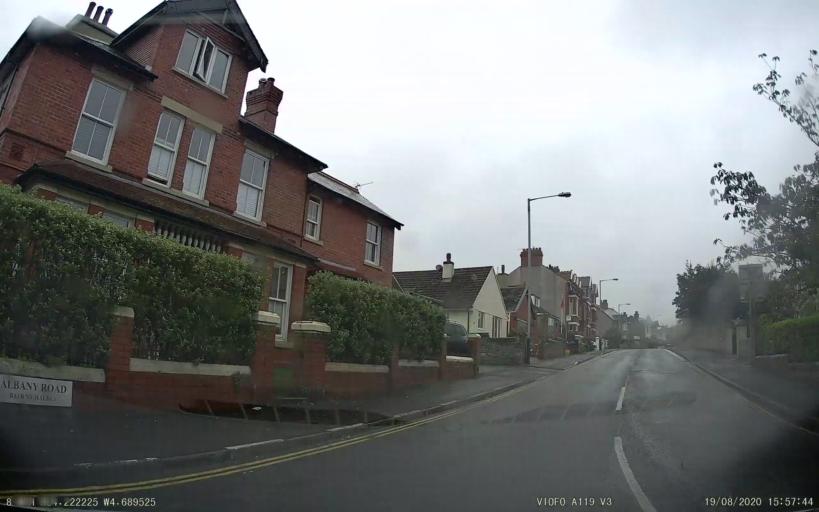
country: IM
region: Port Erin
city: Port Erin
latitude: 54.2222
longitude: -4.6895
